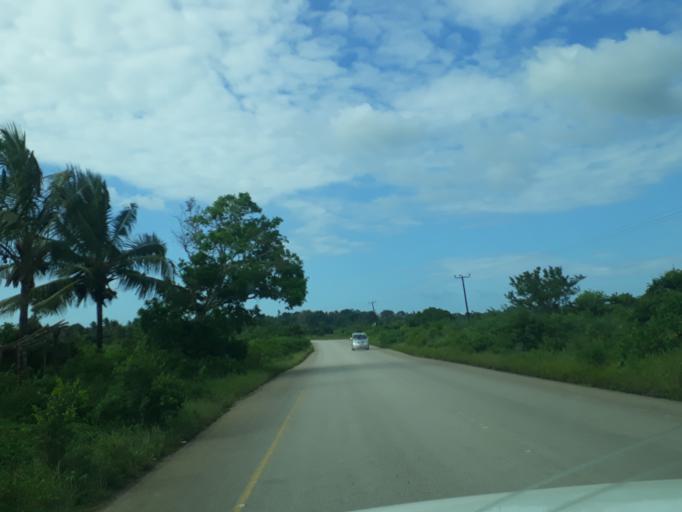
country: TZ
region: Zanzibar North
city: Kijini
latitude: -5.8375
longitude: 39.2875
